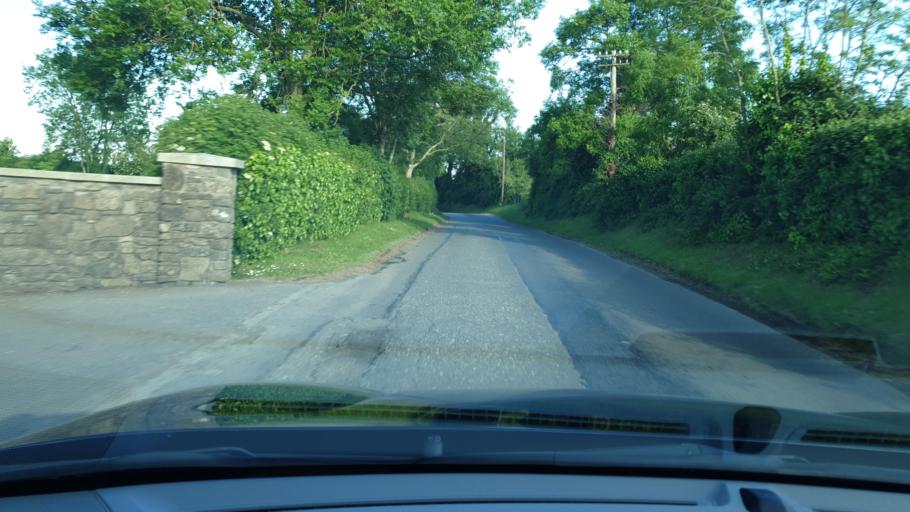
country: IE
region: Leinster
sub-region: An Mhi
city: Ashbourne
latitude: 53.5396
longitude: -6.3400
